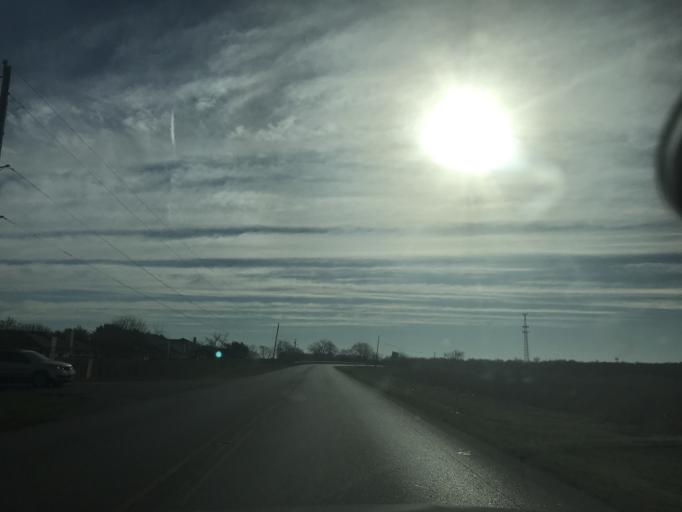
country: US
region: Texas
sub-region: Travis County
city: Manor
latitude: 30.3360
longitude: -97.5523
